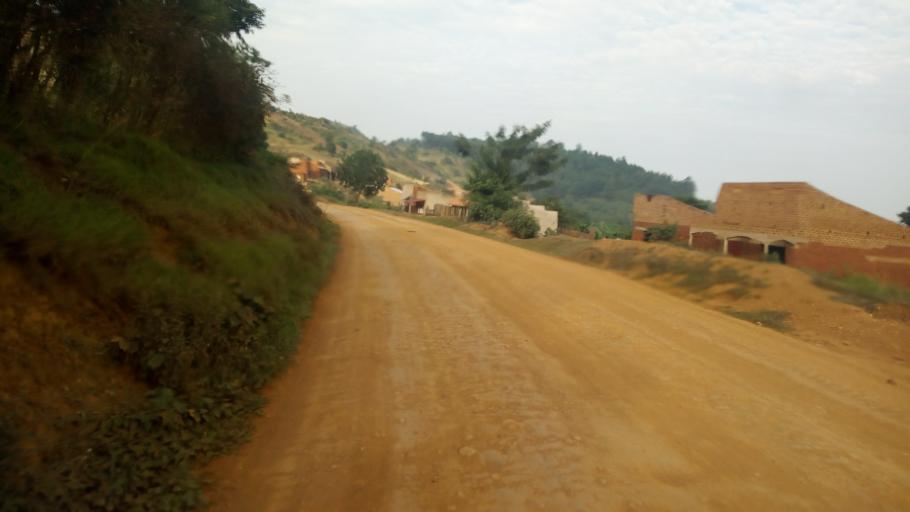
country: UG
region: Western Region
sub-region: Kanungu District
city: Ntungamo
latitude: -0.8287
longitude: 29.6994
